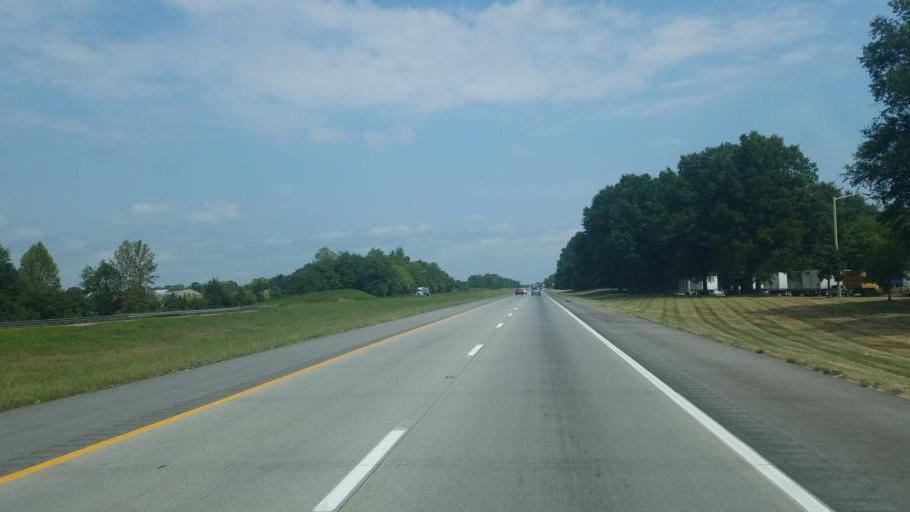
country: US
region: North Carolina
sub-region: Yadkin County
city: Jonesville
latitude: 36.1045
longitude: -80.8128
